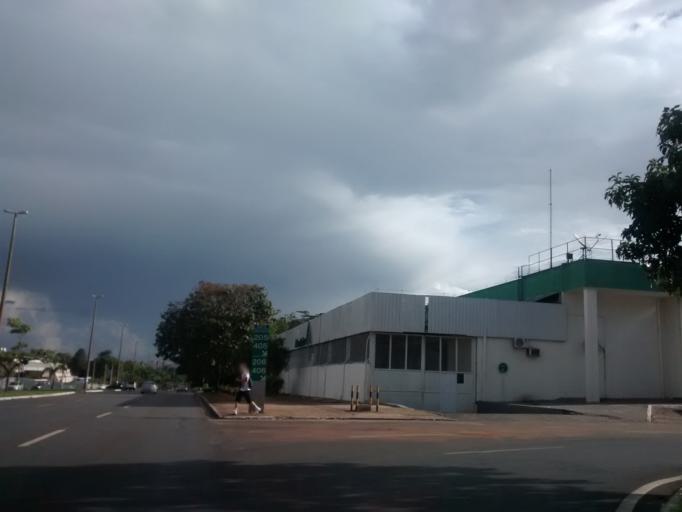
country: BR
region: Federal District
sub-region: Brasilia
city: Brasilia
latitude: -15.7726
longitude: -47.8749
